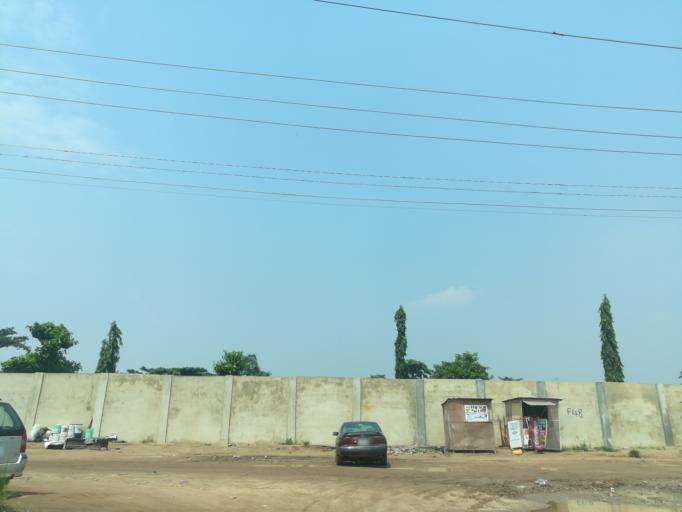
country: NG
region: Lagos
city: Ikorodu
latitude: 6.6342
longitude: 3.4826
